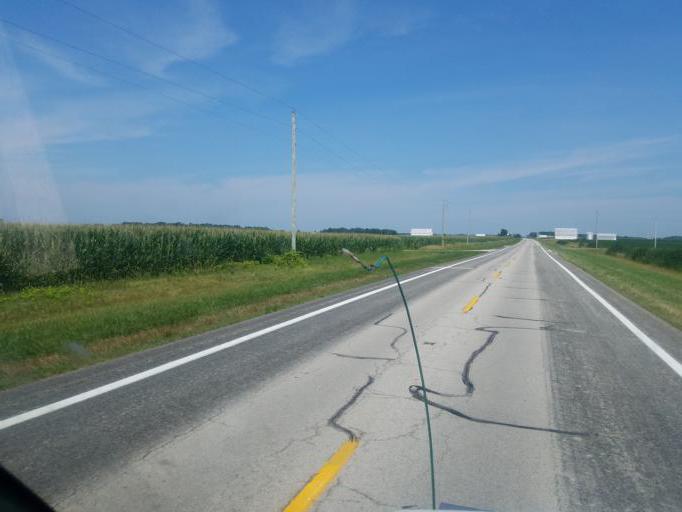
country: US
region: Ohio
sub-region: Auglaize County
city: Saint Marys
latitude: 40.4949
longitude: -84.4294
